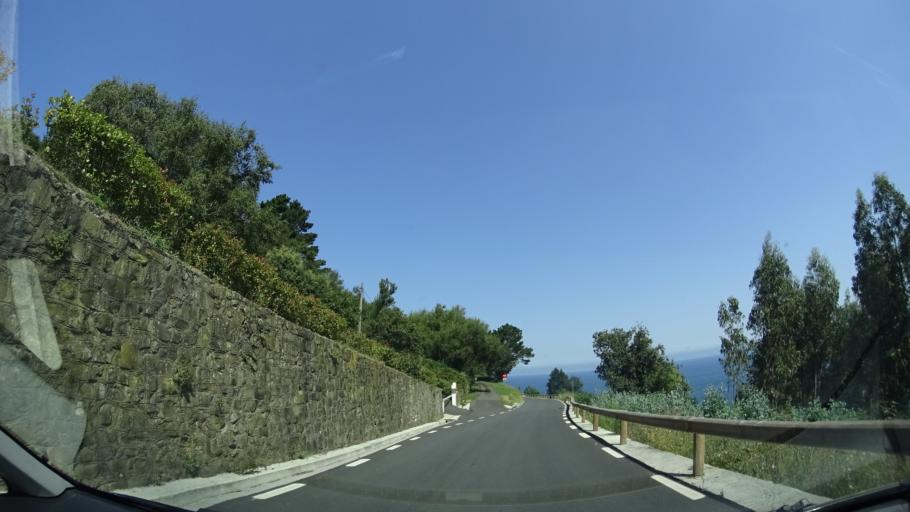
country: ES
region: Basque Country
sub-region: Bizkaia
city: Bermeo
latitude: 43.4524
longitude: -2.7508
